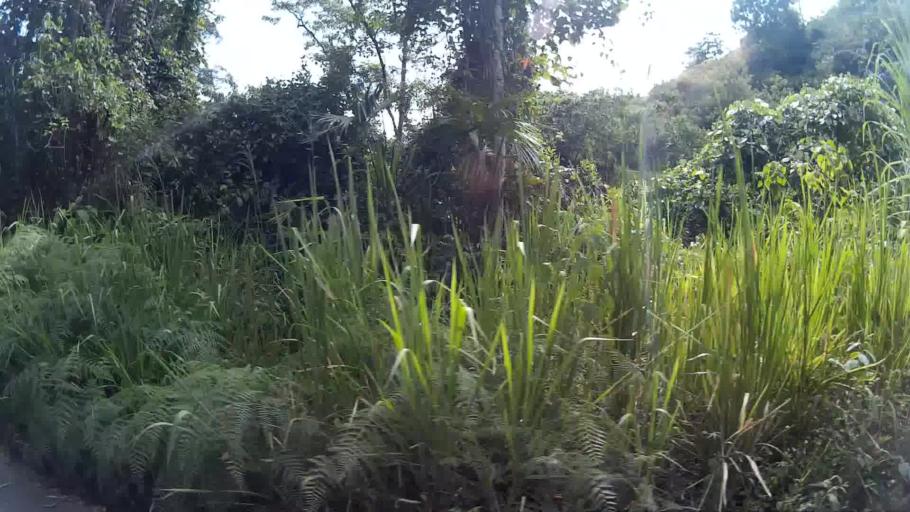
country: CO
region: Caldas
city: Belalcazar
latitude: 4.9451
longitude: -75.8386
